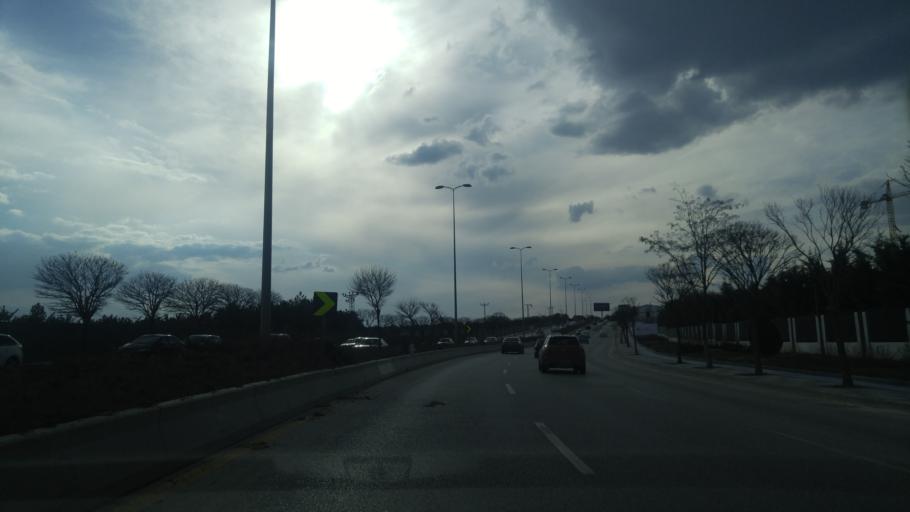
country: TR
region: Ankara
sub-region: Goelbasi
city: Golbasi
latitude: 39.8437
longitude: 32.7883
